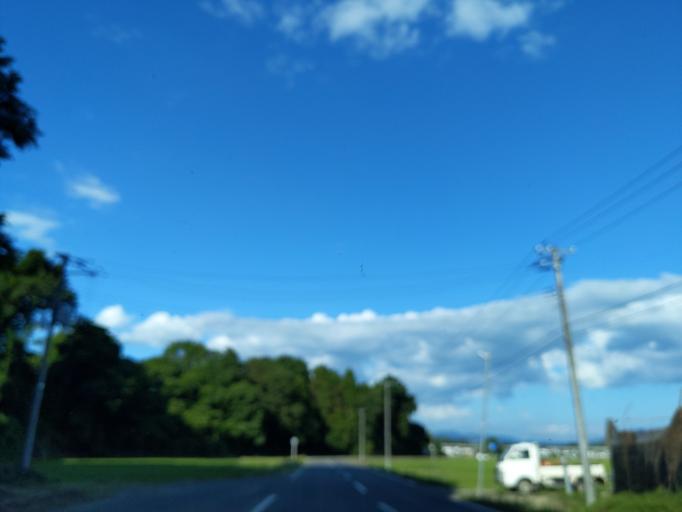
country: JP
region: Fukushima
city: Sukagawa
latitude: 37.3246
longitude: 140.3476
